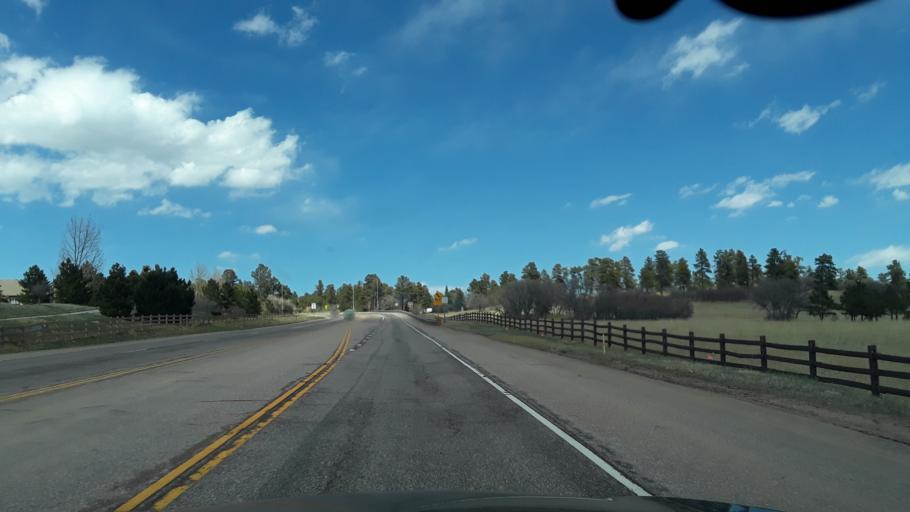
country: US
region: Colorado
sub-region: El Paso County
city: Gleneagle
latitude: 39.0330
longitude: -104.7762
